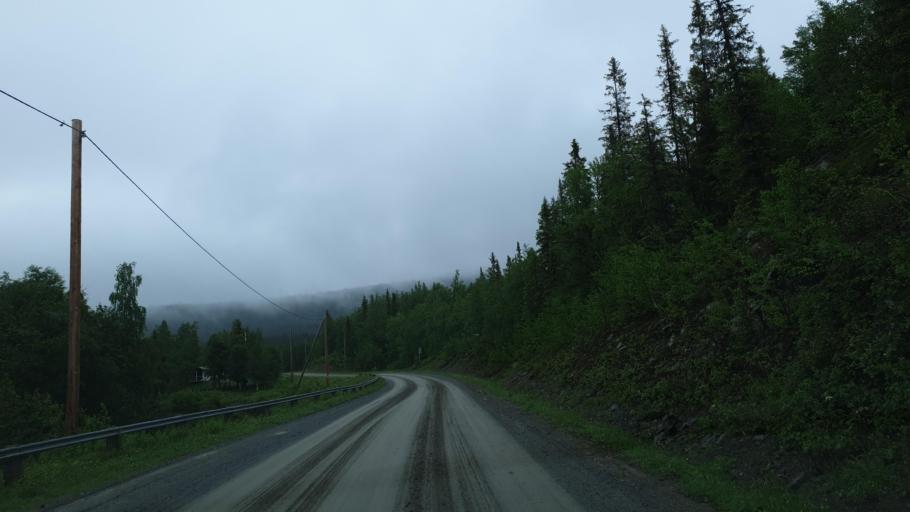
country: SE
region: Vaesterbotten
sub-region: Vilhelmina Kommun
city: Sjoberg
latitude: 65.3338
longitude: 15.8698
